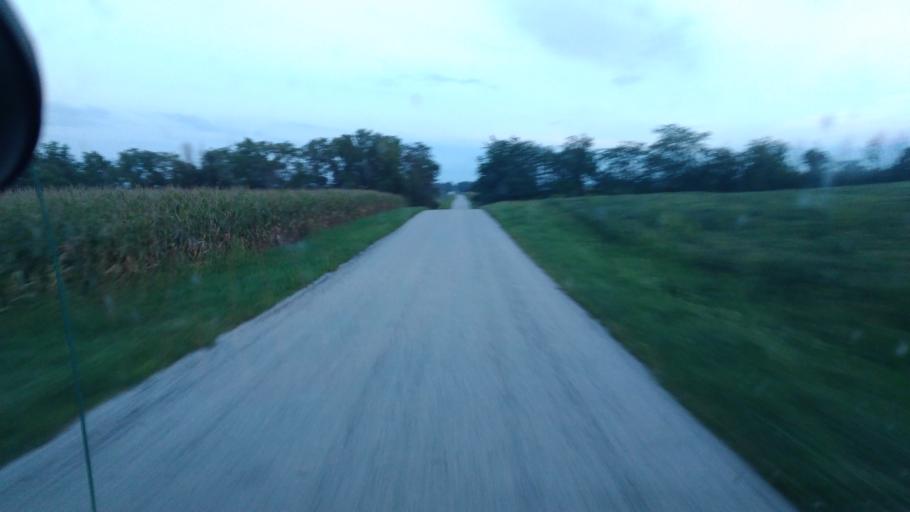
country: US
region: Ohio
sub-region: Hardin County
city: Forest
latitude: 40.6672
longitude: -83.4594
